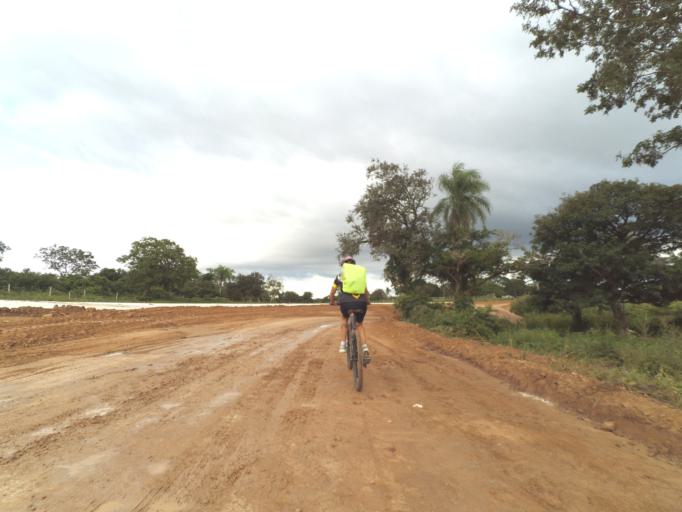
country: BO
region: Santa Cruz
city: Santa Cruz de la Sierra
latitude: -17.7132
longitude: -63.2746
